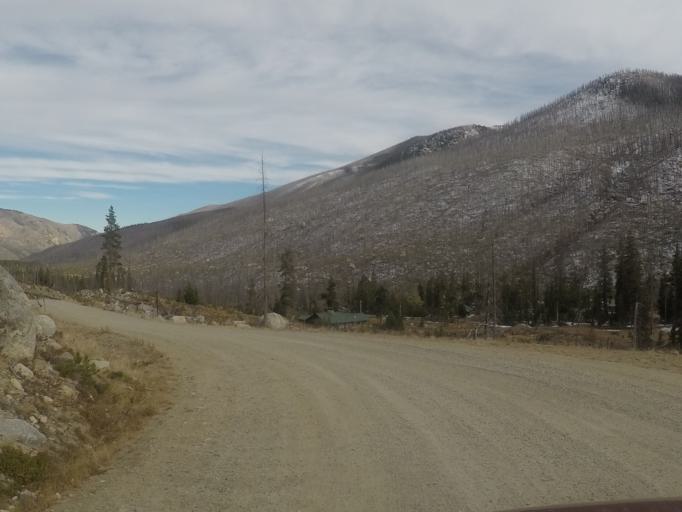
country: US
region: Montana
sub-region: Carbon County
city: Red Lodge
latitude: 45.1726
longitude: -109.4747
